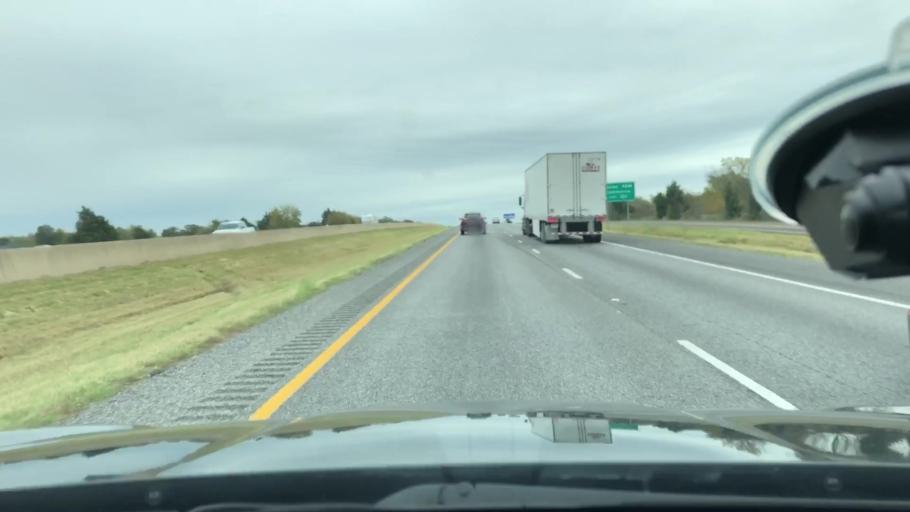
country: US
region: Texas
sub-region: Hunt County
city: Greenville
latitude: 33.1319
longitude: -96.0116
